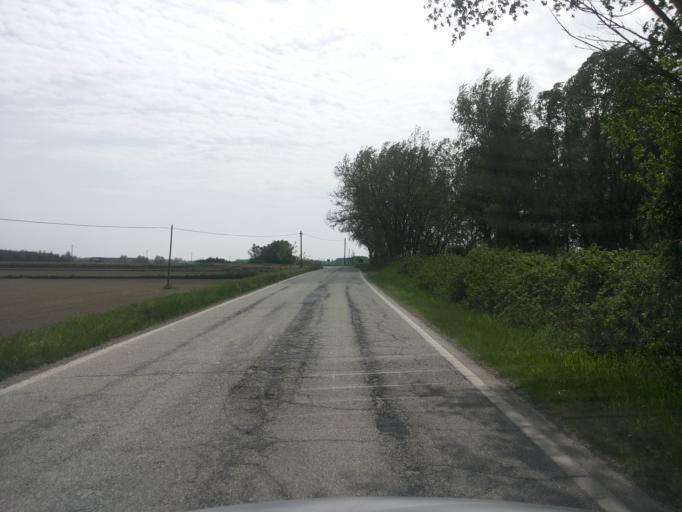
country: IT
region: Piedmont
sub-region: Provincia di Vercelli
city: Caresana
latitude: 45.2103
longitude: 8.5079
